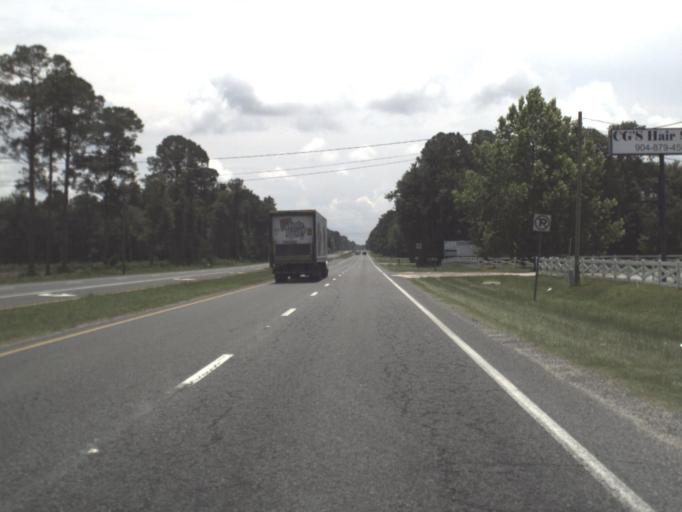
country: US
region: Florida
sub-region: Nassau County
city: Callahan
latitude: 30.5477
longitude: -81.8184
